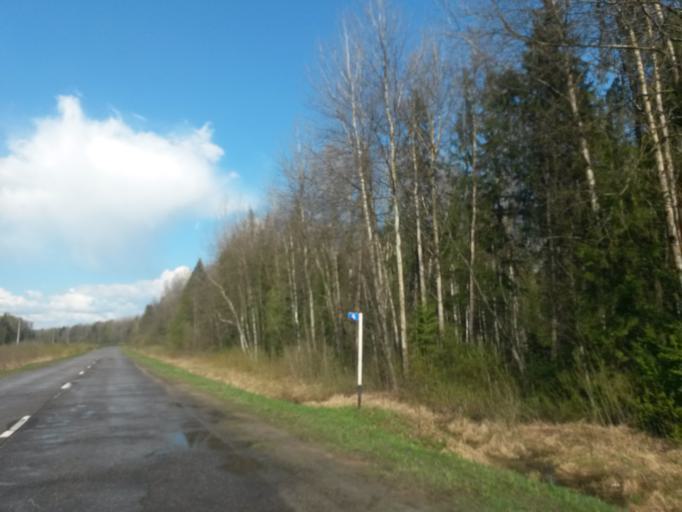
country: RU
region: Jaroslavl
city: Tutayev
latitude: 57.9525
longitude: 39.5003
